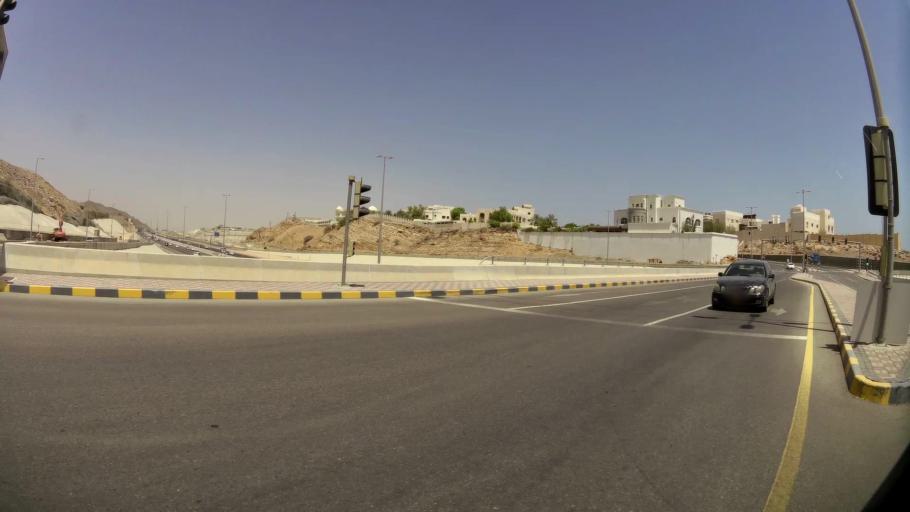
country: OM
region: Muhafazat Masqat
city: Bawshar
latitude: 23.5973
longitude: 58.4788
